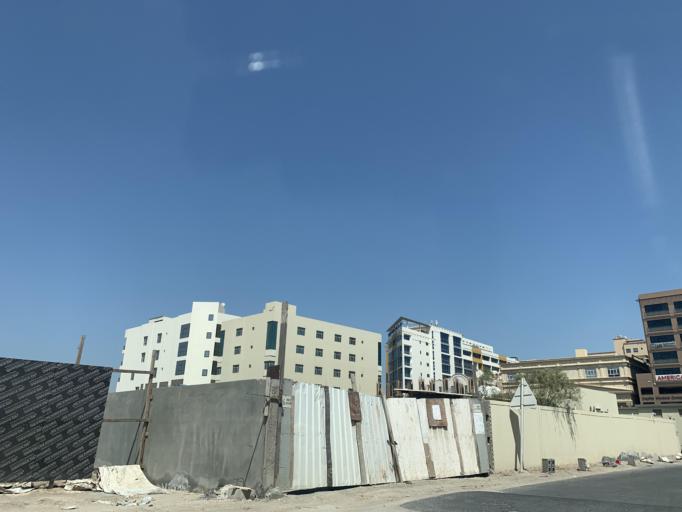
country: BH
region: Manama
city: Manama
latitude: 26.2111
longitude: 50.5744
